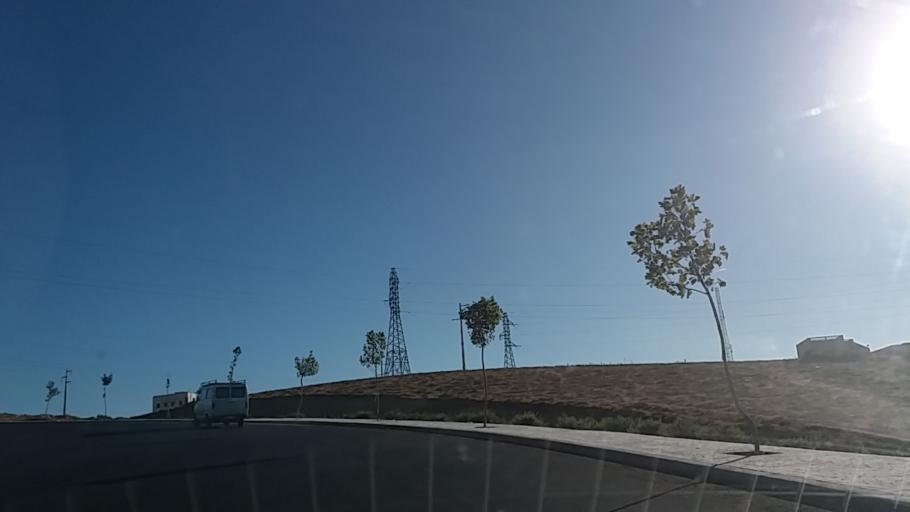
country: MA
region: Tanger-Tetouan
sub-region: Tanger-Assilah
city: Tangier
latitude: 35.7362
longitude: -5.7878
